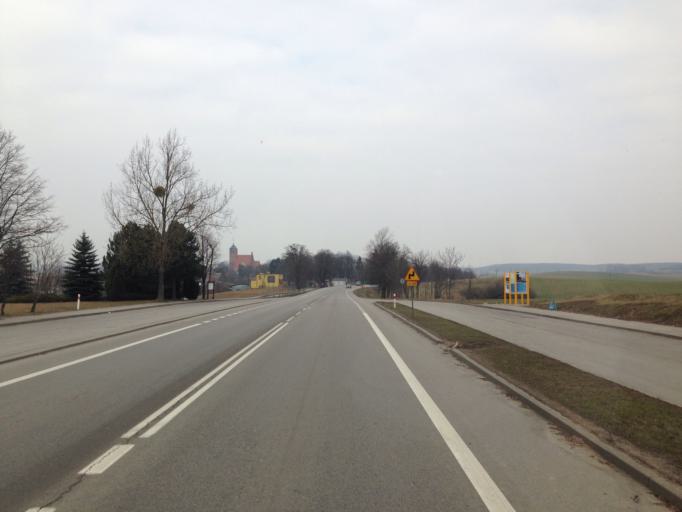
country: PL
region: Pomeranian Voivodeship
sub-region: Powiat tczewski
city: Gniew
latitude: 53.7976
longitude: 18.7781
